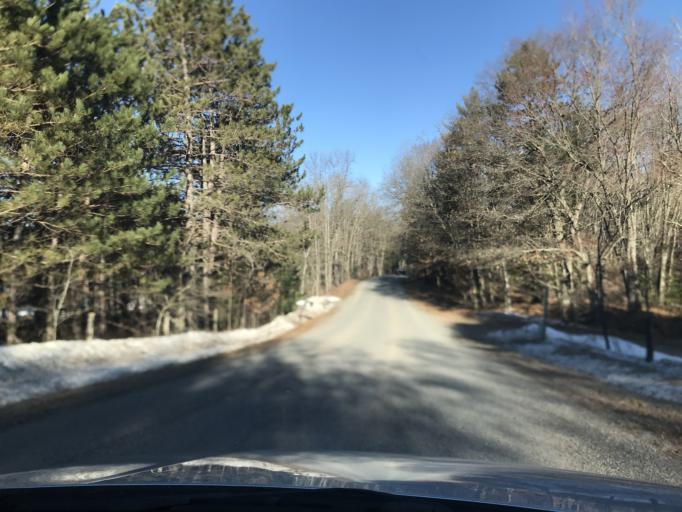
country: US
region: Wisconsin
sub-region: Marinette County
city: Niagara
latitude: 45.3901
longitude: -88.0504
